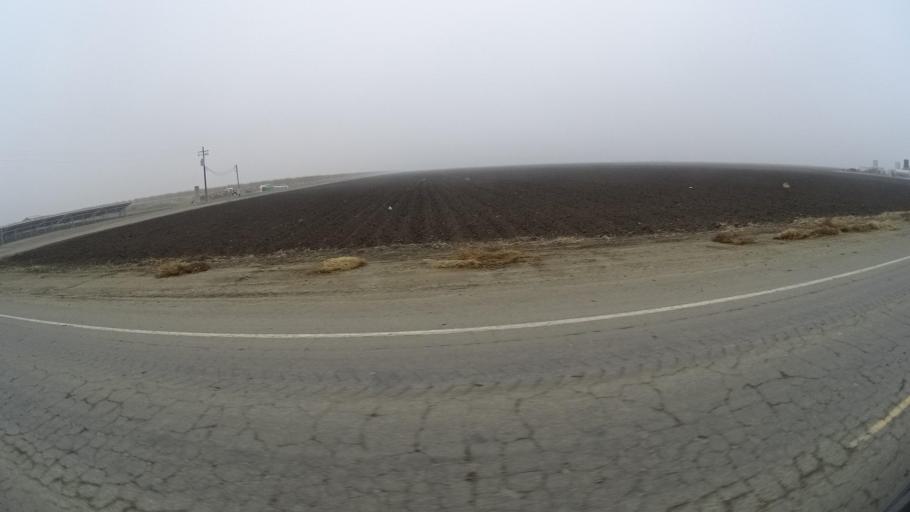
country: US
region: California
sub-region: Kern County
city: Buttonwillow
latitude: 35.4357
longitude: -119.5181
